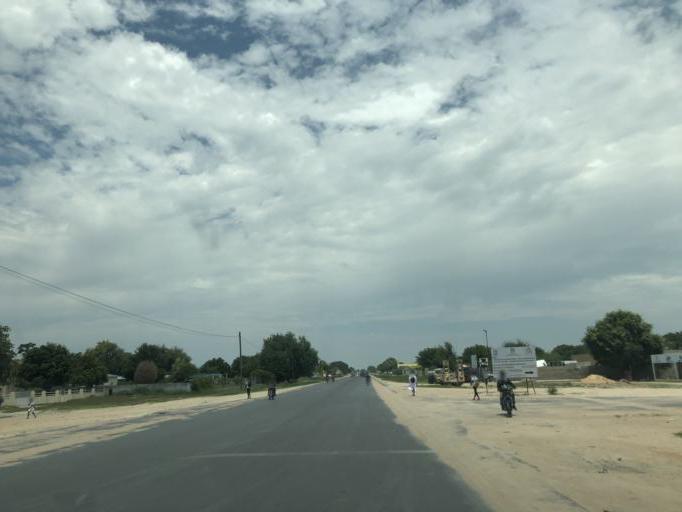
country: AO
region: Cunene
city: Ondjiva
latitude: -17.0887
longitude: 15.7435
